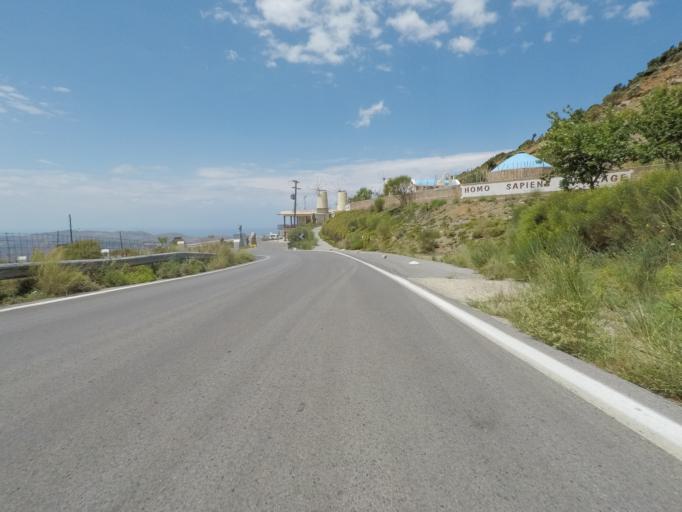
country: GR
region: Crete
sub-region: Nomos Irakleiou
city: Mokhos
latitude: 35.2147
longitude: 25.4611
